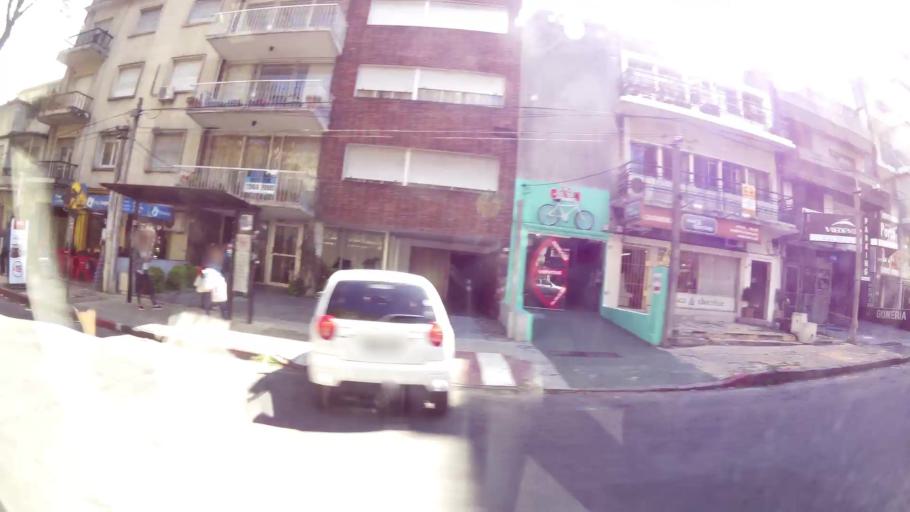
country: UY
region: Montevideo
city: Montevideo
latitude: -34.9097
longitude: -56.1530
